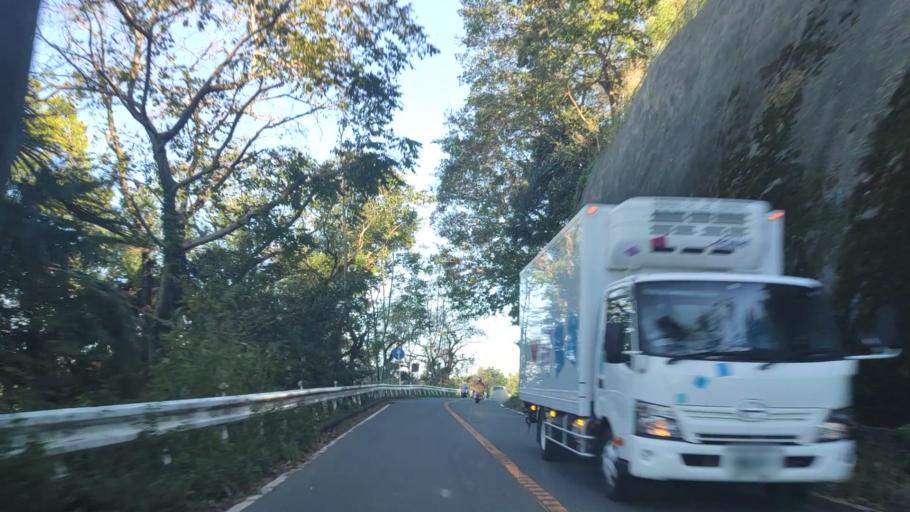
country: JP
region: Kanagawa
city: Zama
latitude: 35.5307
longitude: 139.3443
